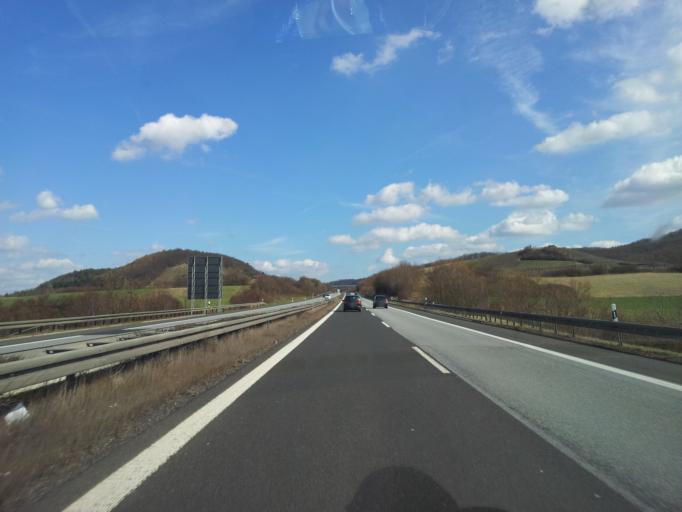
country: DE
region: Bavaria
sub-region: Regierungsbezirk Unterfranken
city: Sand
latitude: 49.9764
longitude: 10.5697
